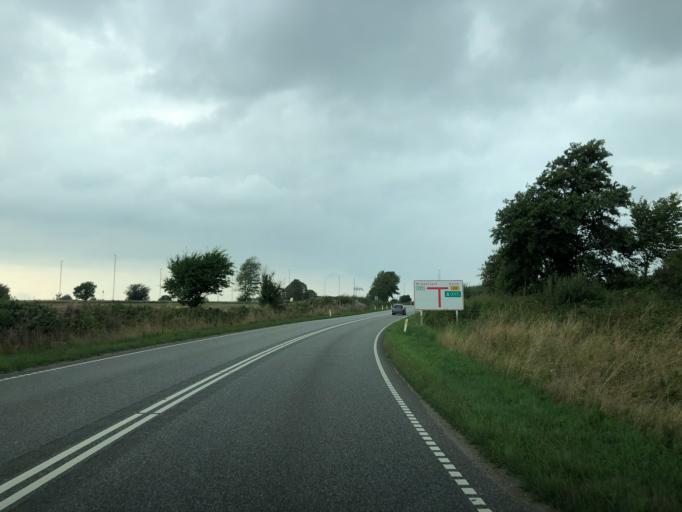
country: DK
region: South Denmark
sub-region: Vejle Kommune
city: Vejle
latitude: 55.6695
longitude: 9.5876
